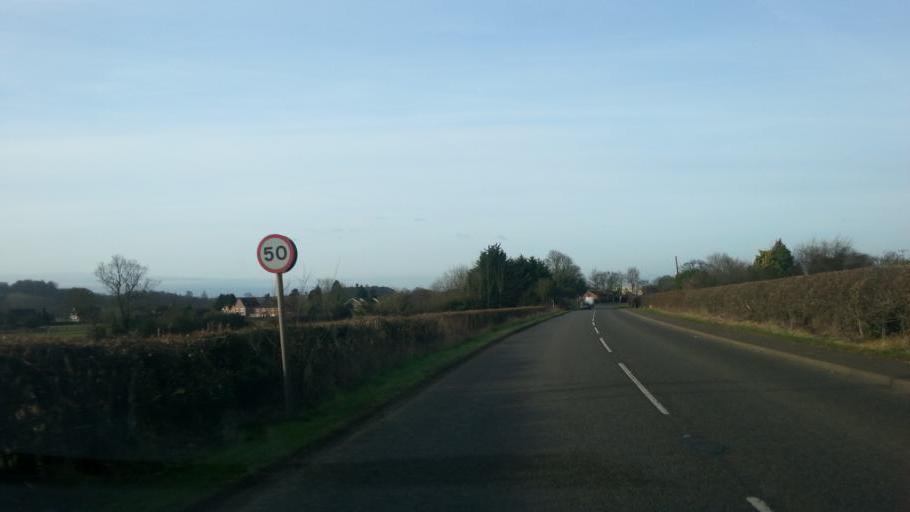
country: GB
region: England
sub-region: Lincolnshire
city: Barrowby
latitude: 52.8861
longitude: -0.6907
